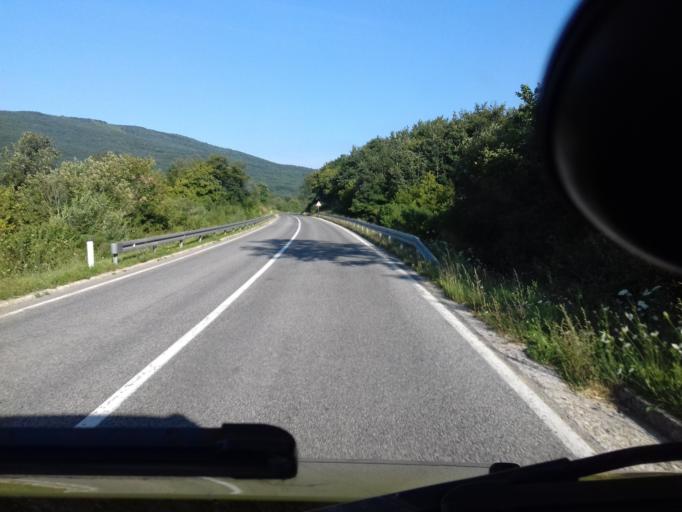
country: BA
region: Federation of Bosnia and Herzegovina
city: Orasac
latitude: 44.6623
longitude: 16.1451
